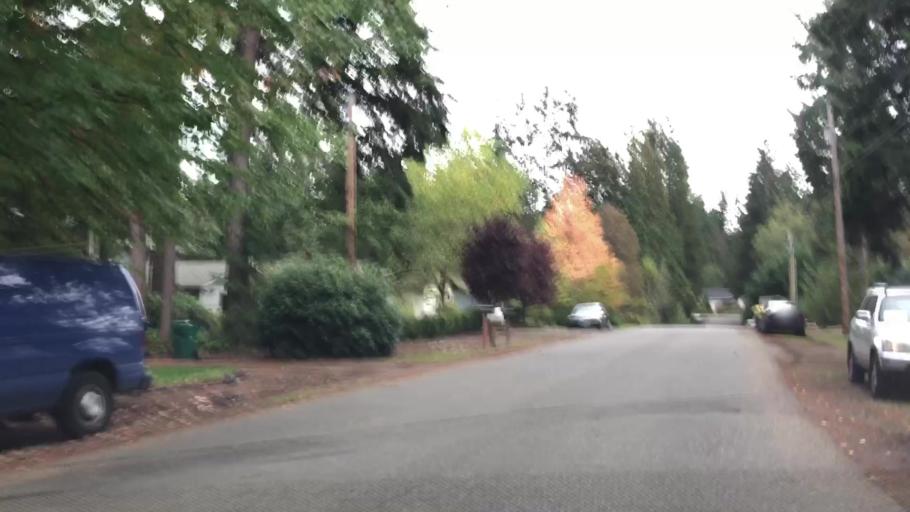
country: US
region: Washington
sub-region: King County
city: Cottage Lake
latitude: 47.7424
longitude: -122.0924
